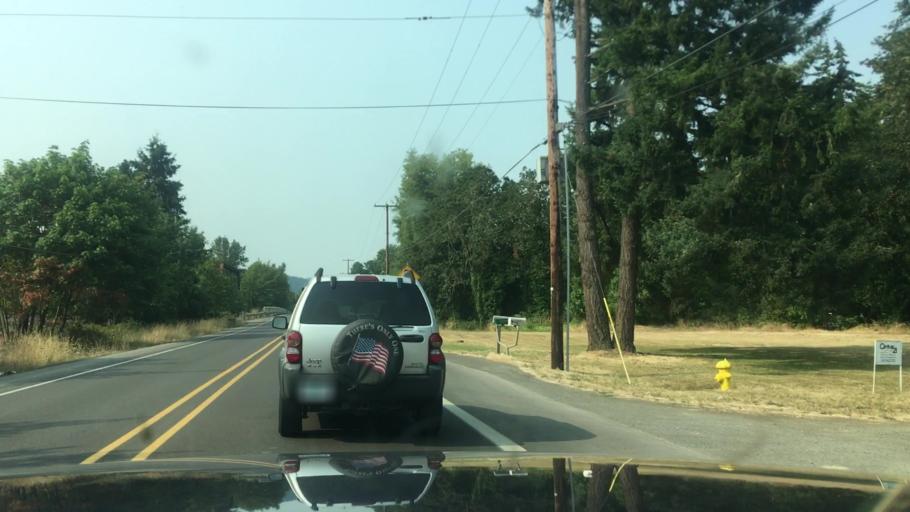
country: US
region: Oregon
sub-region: Lane County
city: Cottage Grove
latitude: 43.7859
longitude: -123.0673
